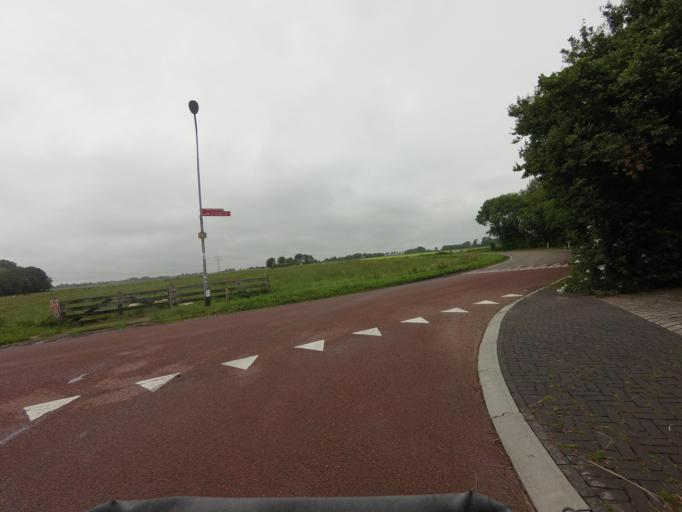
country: NL
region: North Holland
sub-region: Gemeente Schagen
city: Schagen
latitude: 52.7752
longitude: 4.8283
